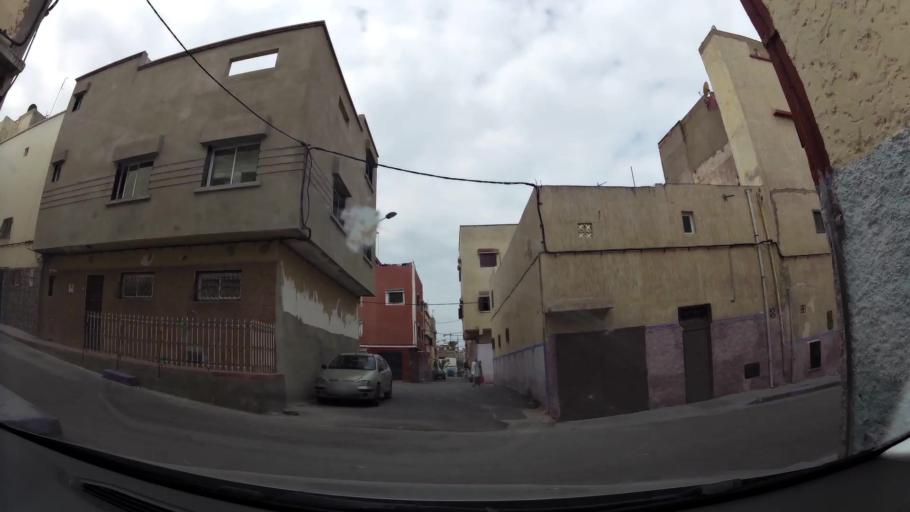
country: MA
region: Rabat-Sale-Zemmour-Zaer
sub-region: Rabat
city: Rabat
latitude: 34.0039
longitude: -6.8703
